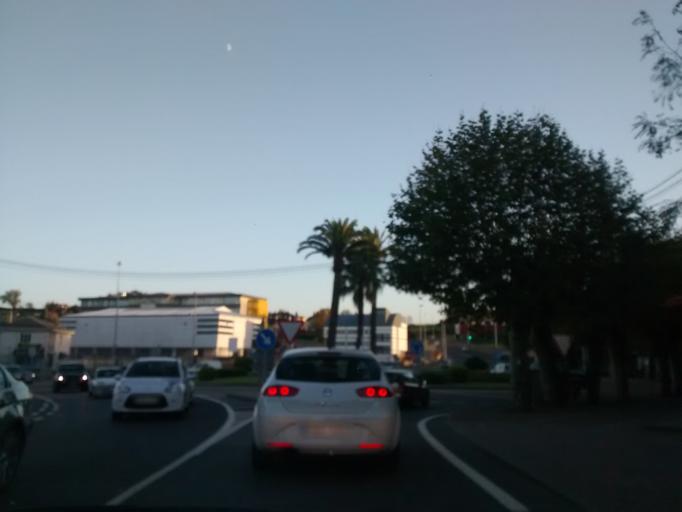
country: ES
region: Cantabria
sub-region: Provincia de Cantabria
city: Santa Cruz de Bezana
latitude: 43.4656
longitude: -3.8677
